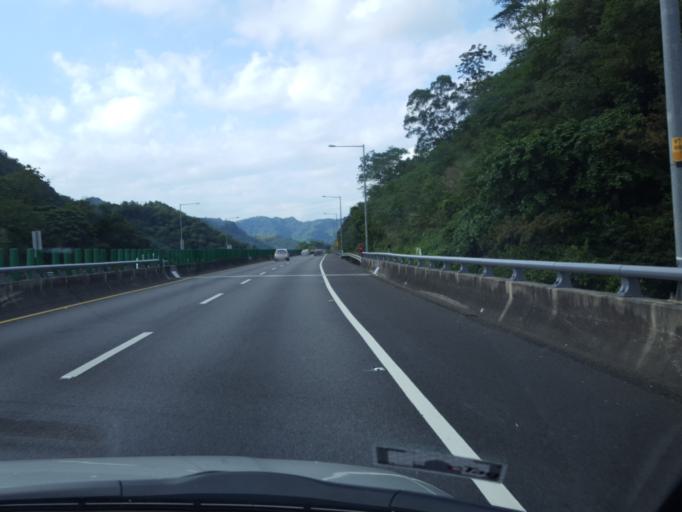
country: TW
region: Taipei
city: Taipei
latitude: 24.9841
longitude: 121.6611
